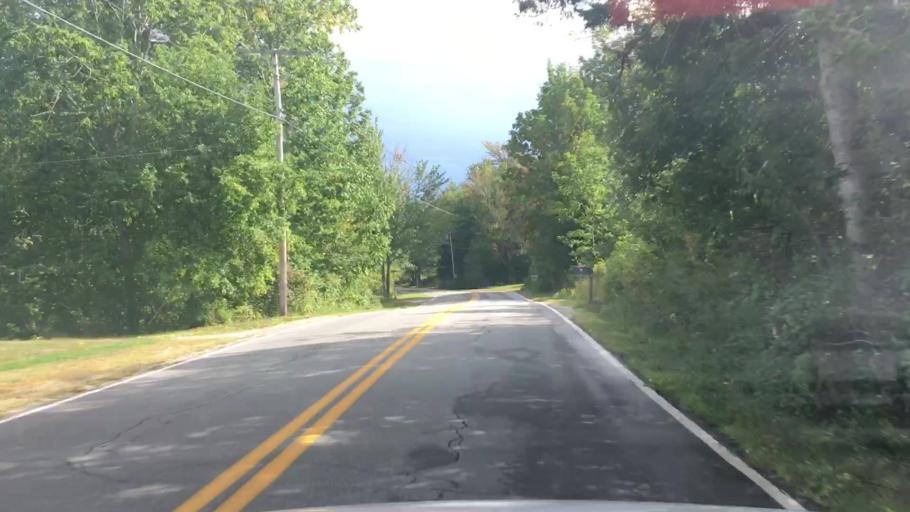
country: US
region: Maine
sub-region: Hancock County
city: Trenton
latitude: 44.4335
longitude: -68.3979
